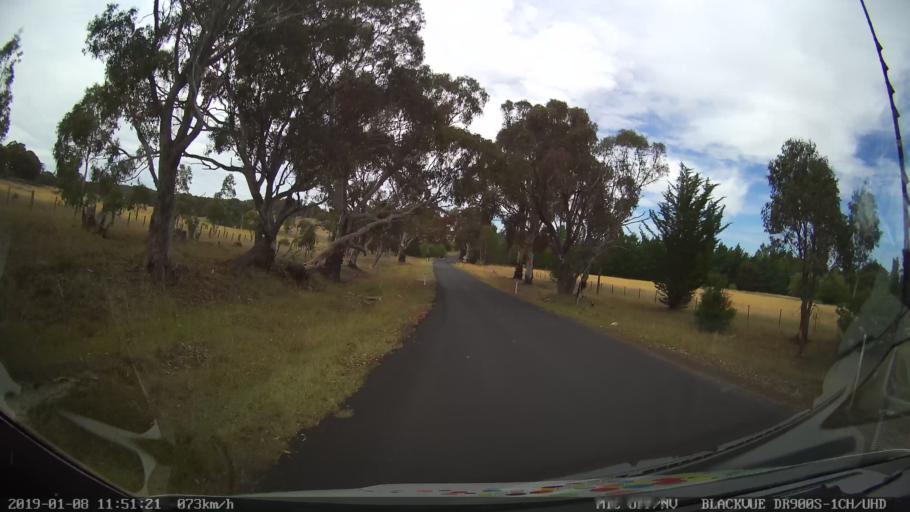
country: AU
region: New South Wales
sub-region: Armidale Dumaresq
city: Armidale
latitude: -30.3921
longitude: 151.5594
